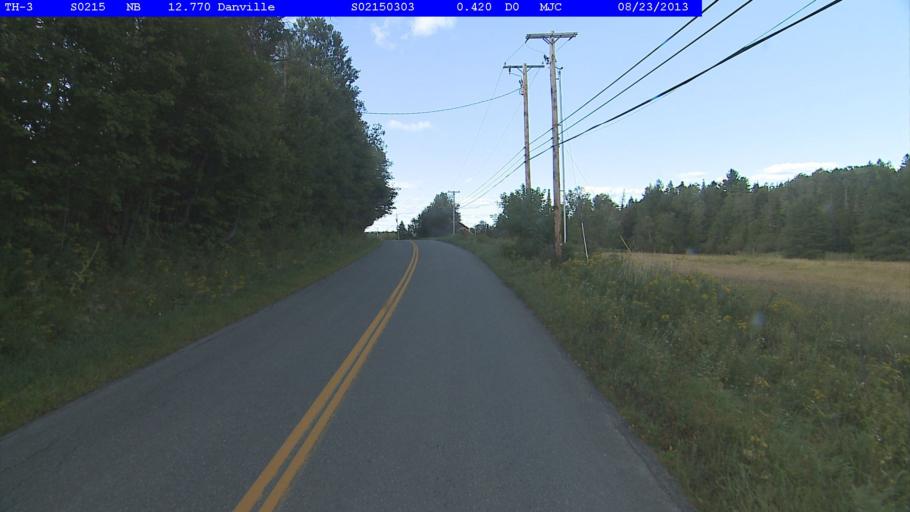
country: US
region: Vermont
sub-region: Caledonia County
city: Saint Johnsbury
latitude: 44.3717
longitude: -72.1463
